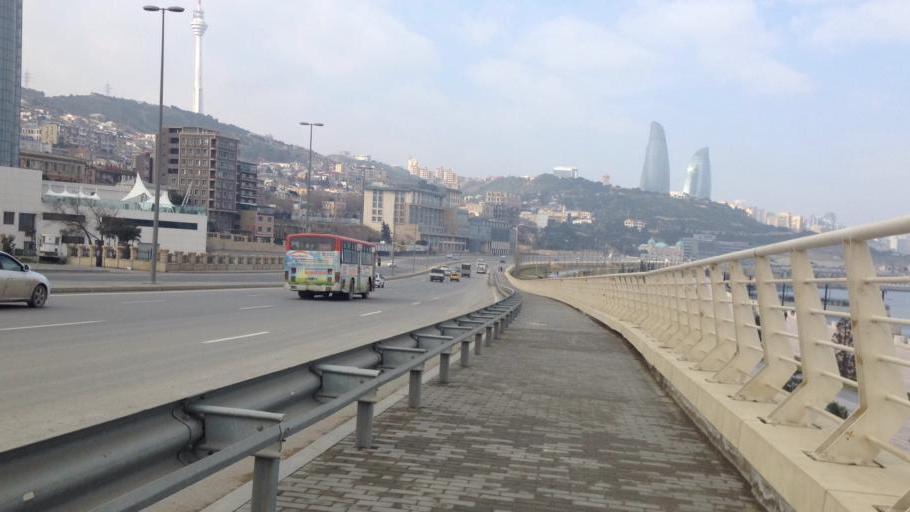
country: AZ
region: Baki
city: Badamdar
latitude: 40.3459
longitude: 49.8405
